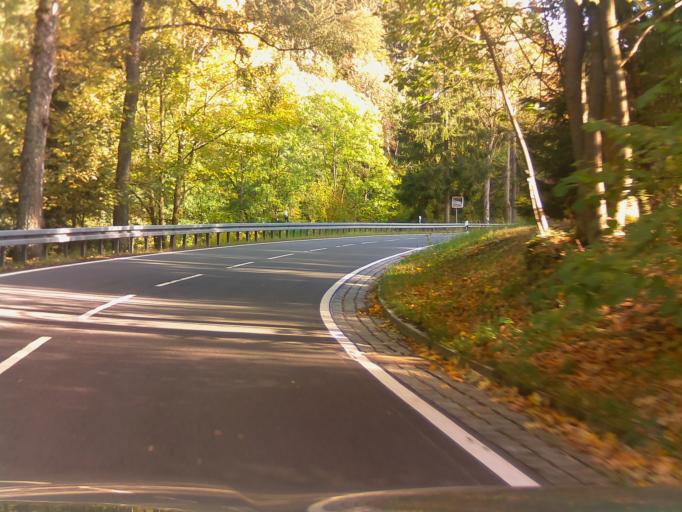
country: DE
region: Thuringia
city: Bermbach
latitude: 50.7015
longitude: 10.6272
